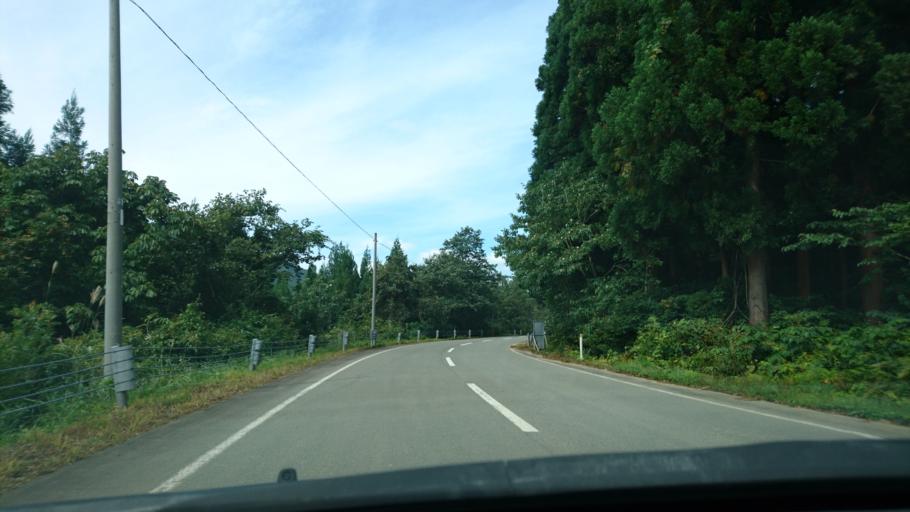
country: JP
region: Akita
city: Yuzawa
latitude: 39.0284
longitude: 140.7279
